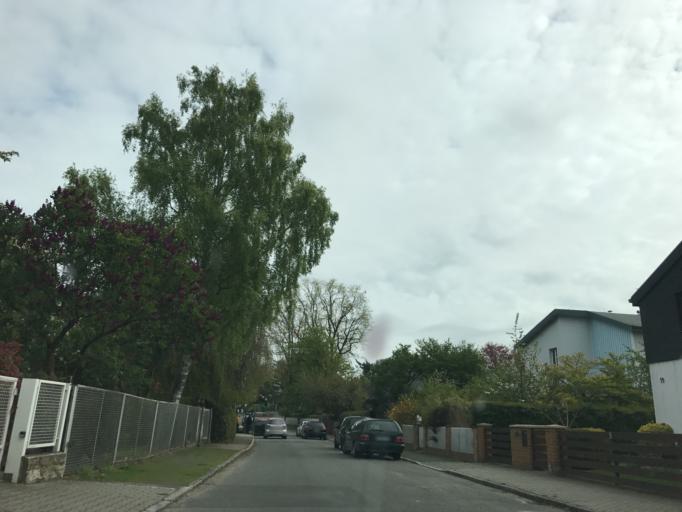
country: DE
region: Berlin
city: Gatow
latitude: 52.5043
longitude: 13.1853
